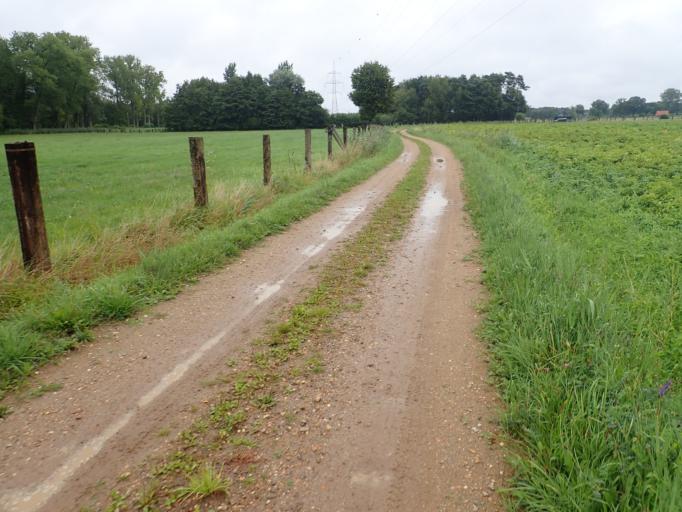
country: BE
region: Flanders
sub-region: Provincie Antwerpen
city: Zoersel
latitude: 51.2470
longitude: 4.7076
